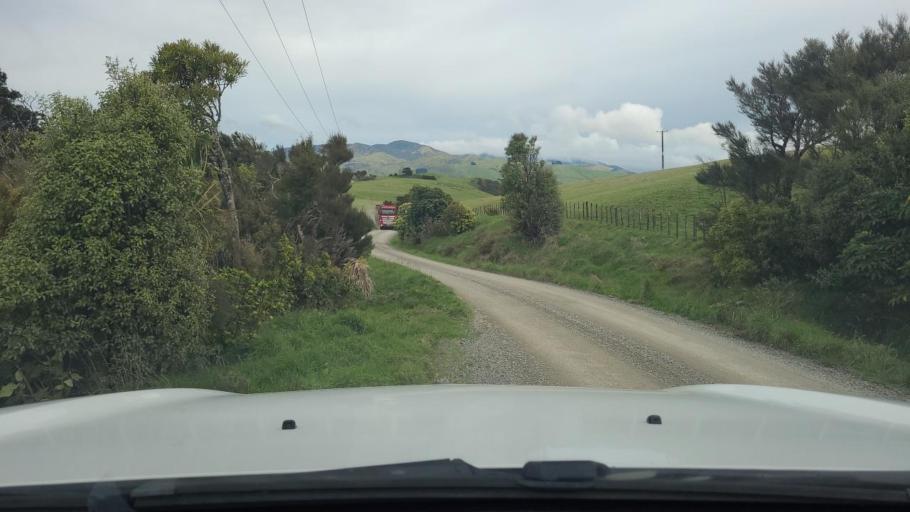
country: NZ
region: Wellington
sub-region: South Wairarapa District
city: Waipawa
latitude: -41.3653
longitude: 175.4860
